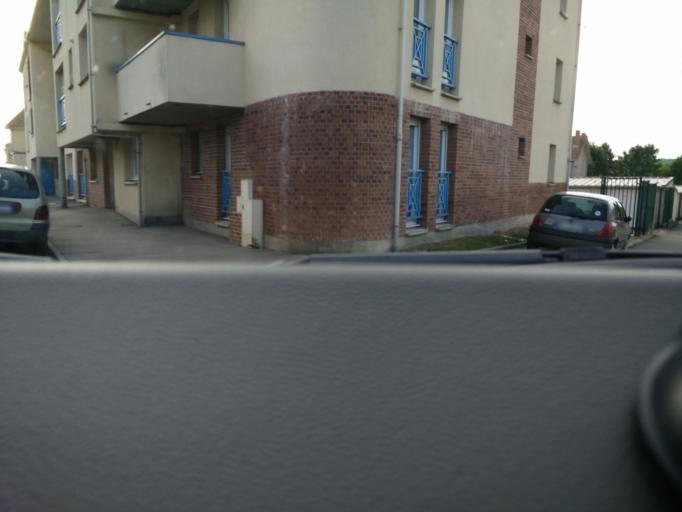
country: FR
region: Nord-Pas-de-Calais
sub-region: Departement du Pas-de-Calais
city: Grenay
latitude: 50.4485
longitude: 2.7492
